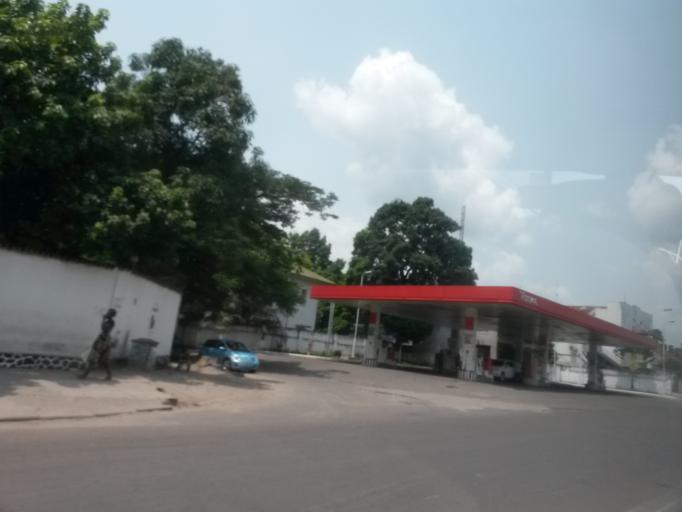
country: CD
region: Kinshasa
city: Kinshasa
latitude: -4.3122
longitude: 15.2894
